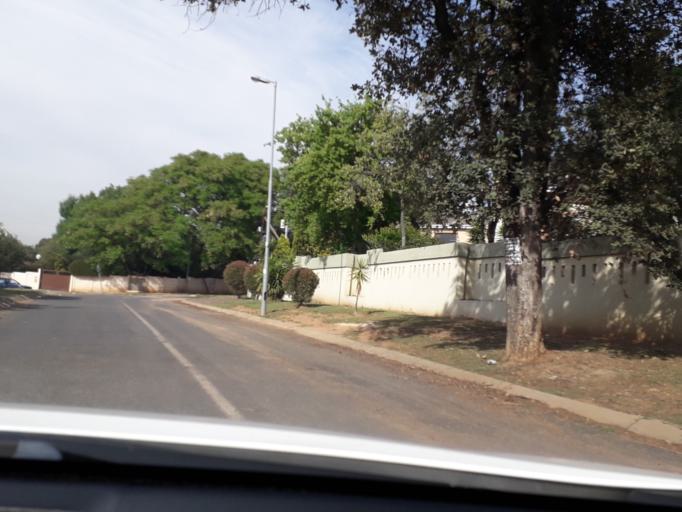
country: ZA
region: Gauteng
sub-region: City of Johannesburg Metropolitan Municipality
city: Modderfontein
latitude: -26.1179
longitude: 28.1072
